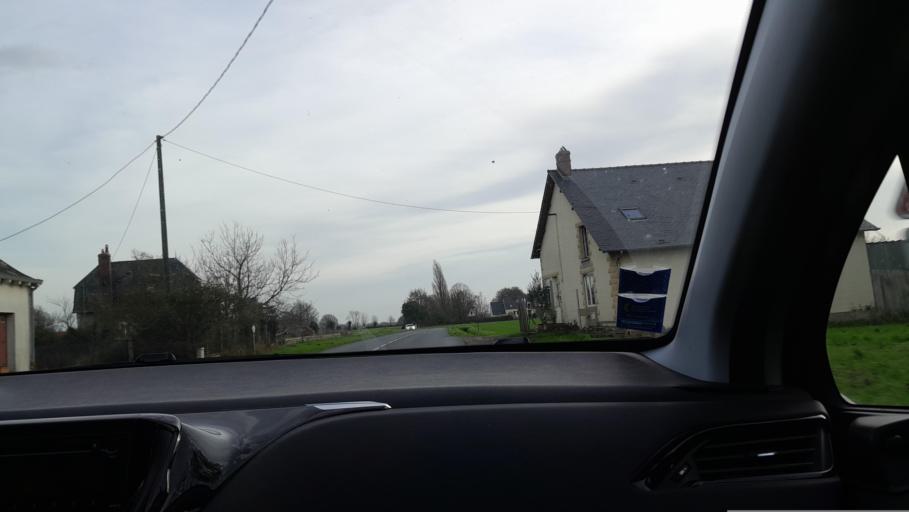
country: FR
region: Brittany
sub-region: Departement d'Ille-et-Vilaine
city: La Guerche-de-Bretagne
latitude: 47.9478
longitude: -1.2065
